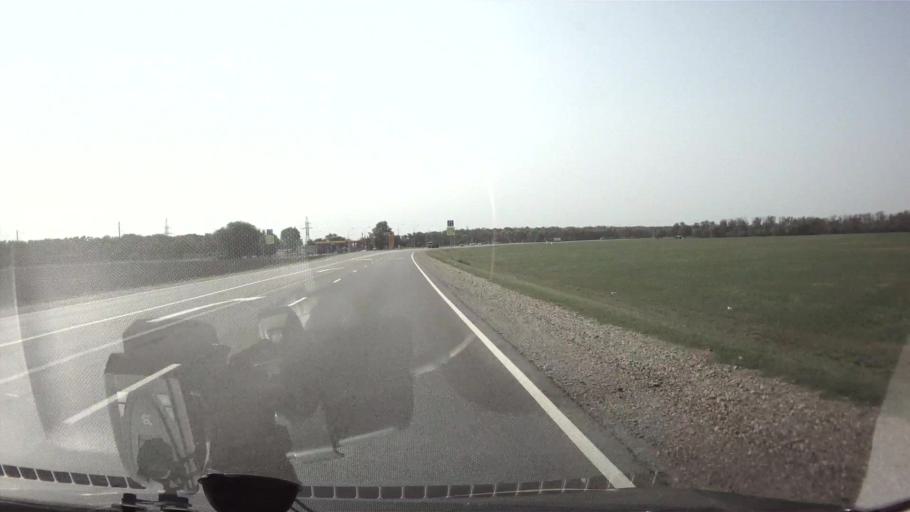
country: RU
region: Krasnodarskiy
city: Tbilisskaya
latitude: 45.3689
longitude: 40.1304
